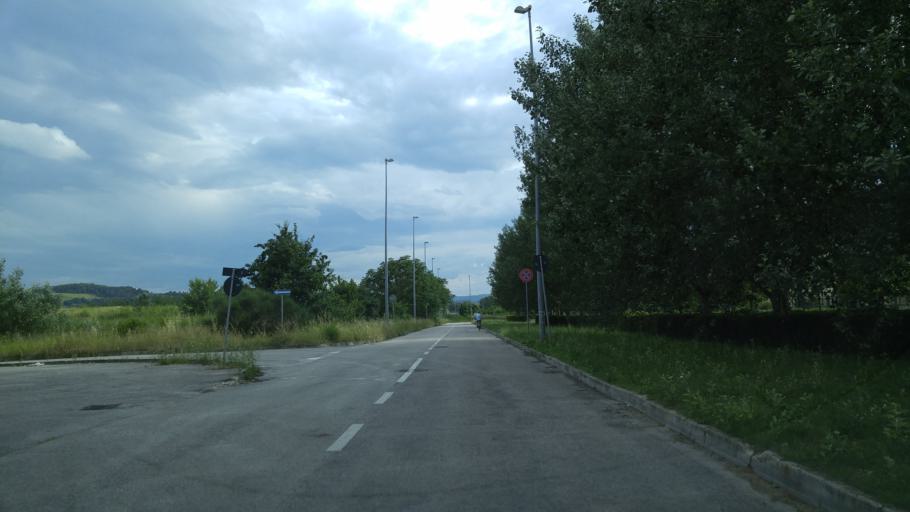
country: IT
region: The Marches
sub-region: Provincia di Pesaro e Urbino
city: Pesaro
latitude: 43.9035
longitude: 12.8690
